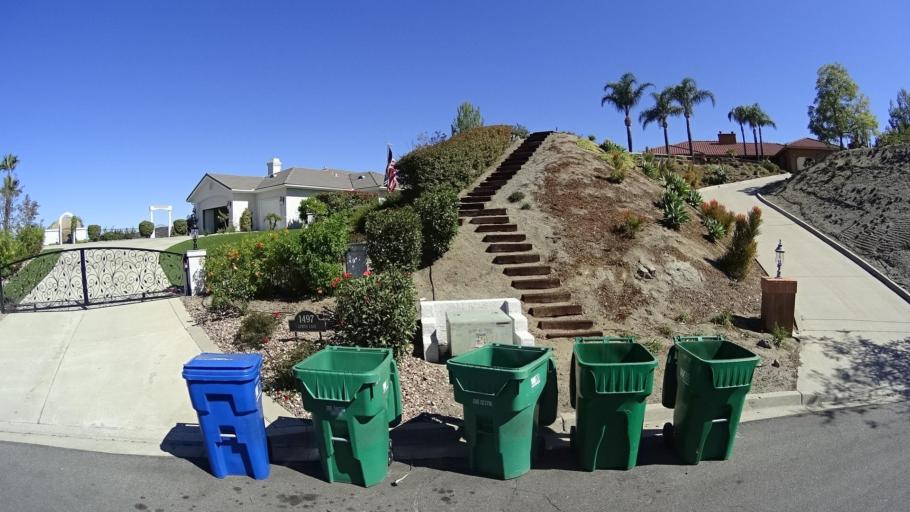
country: US
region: California
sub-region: San Diego County
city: Alpine
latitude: 32.8561
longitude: -116.7655
